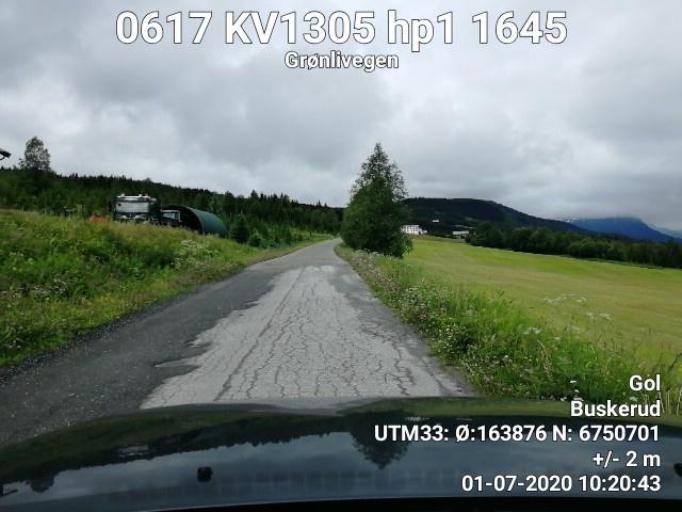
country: NO
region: Buskerud
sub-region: Gol
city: Gol
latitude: 60.7494
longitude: 8.8274
